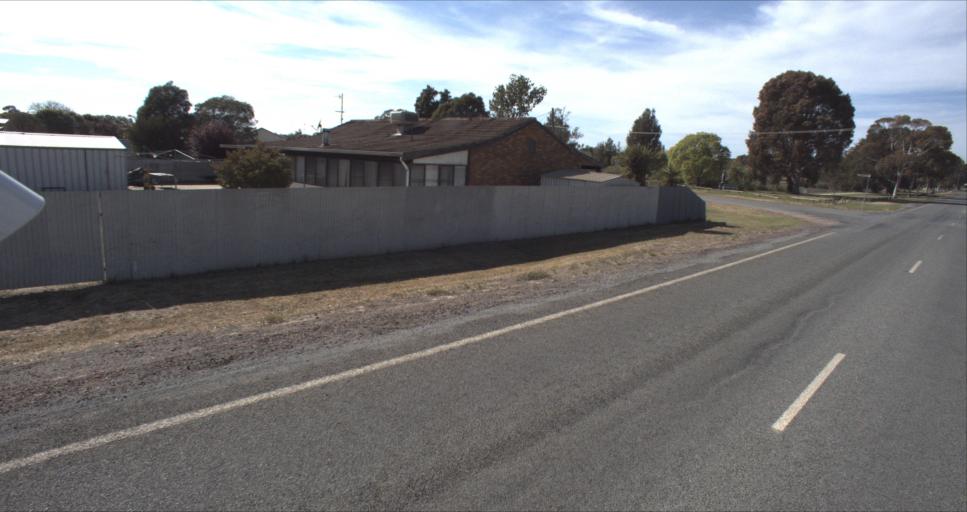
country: AU
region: New South Wales
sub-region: Leeton
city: Leeton
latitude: -34.5982
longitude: 146.4058
